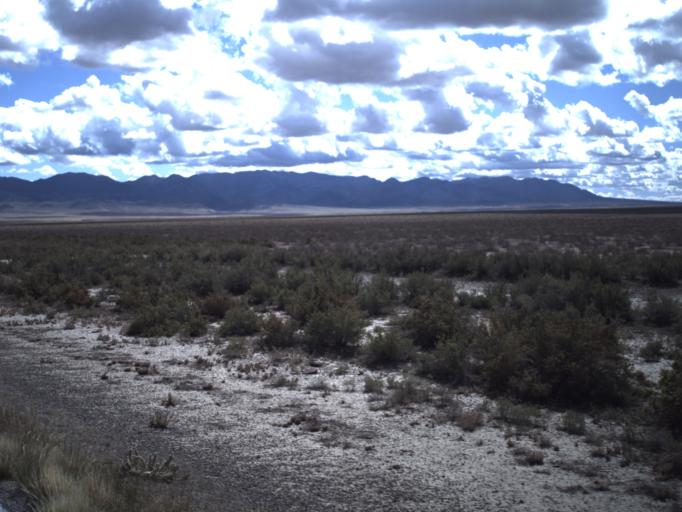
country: US
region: Utah
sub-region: Beaver County
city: Milford
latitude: 38.5485
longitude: -113.7257
